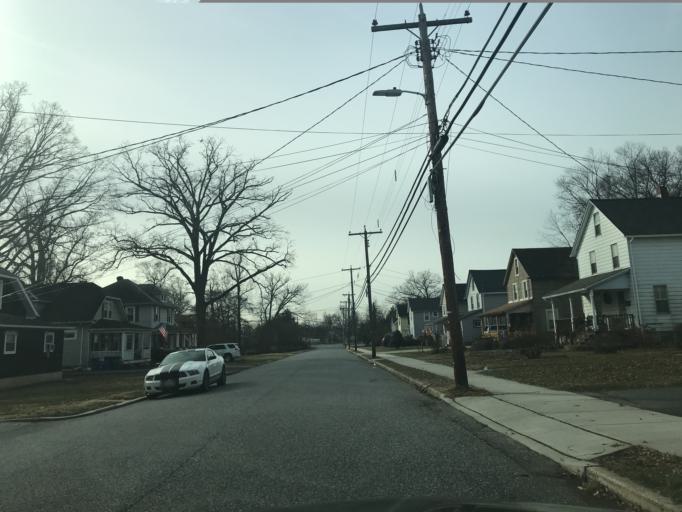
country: US
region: Maryland
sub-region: Harford County
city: Aberdeen
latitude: 39.5131
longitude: -76.1685
